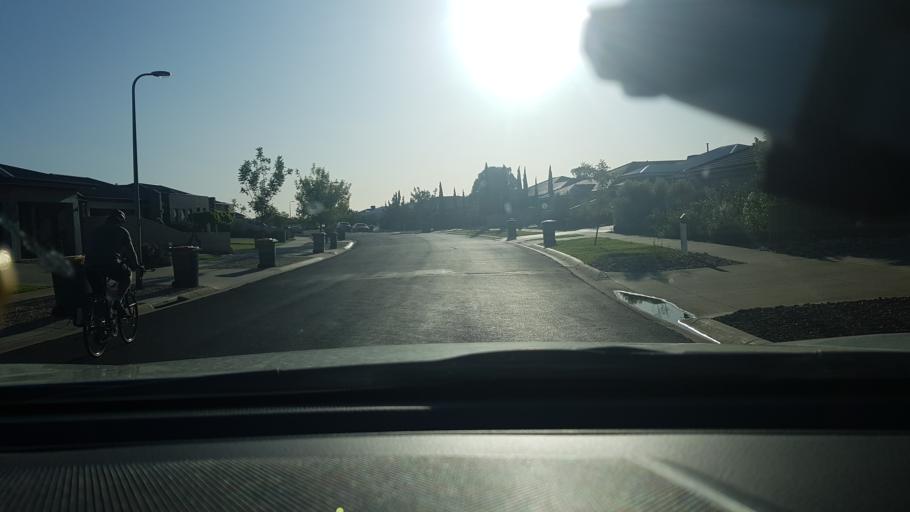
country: AU
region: Victoria
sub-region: Horsham
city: Horsham
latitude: -36.7134
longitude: 142.1790
